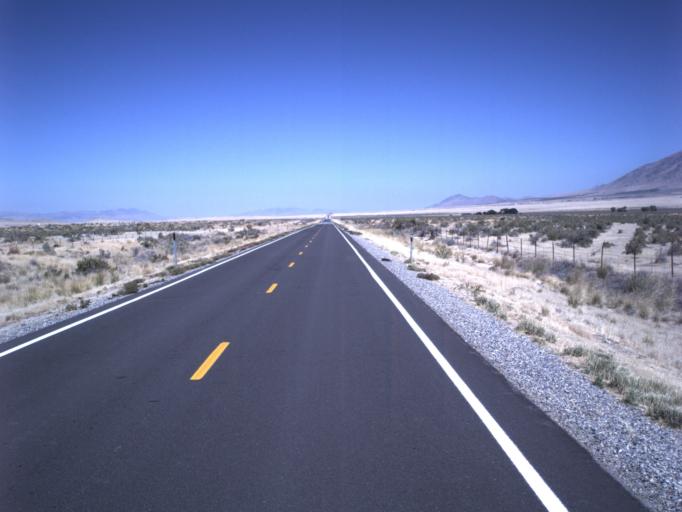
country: US
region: Utah
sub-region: Tooele County
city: Grantsville
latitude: 40.3228
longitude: -112.7439
